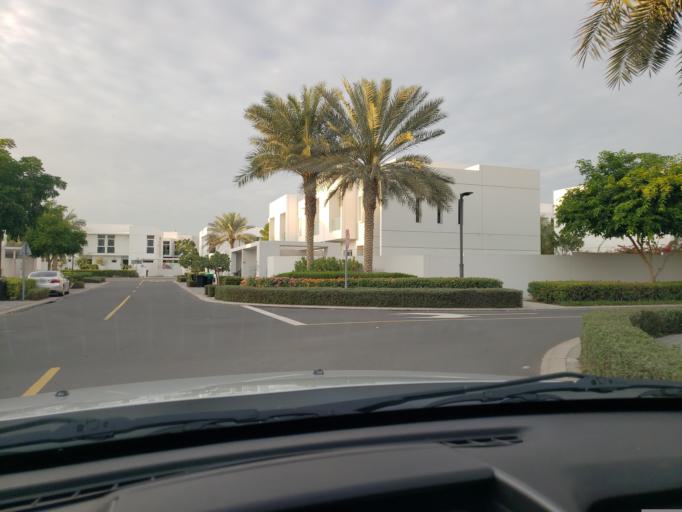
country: AE
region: Dubai
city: Dubai
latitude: 25.0186
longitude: 55.2747
